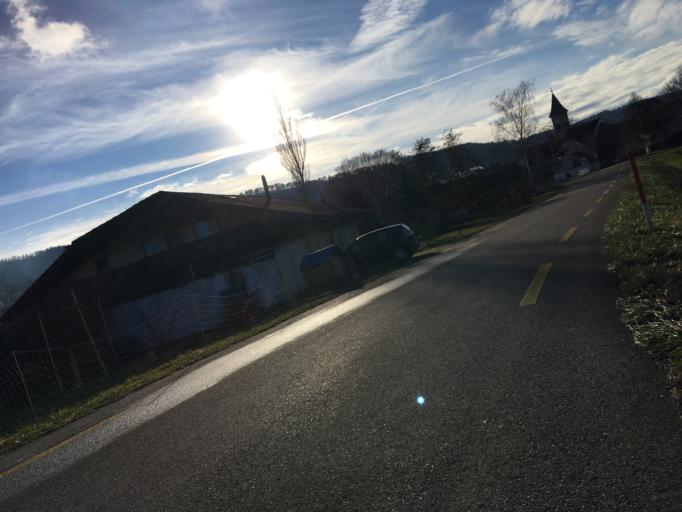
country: DE
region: Baden-Wuerttemberg
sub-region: Freiburg Region
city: Gottmadingen
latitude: 47.7185
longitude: 8.7860
